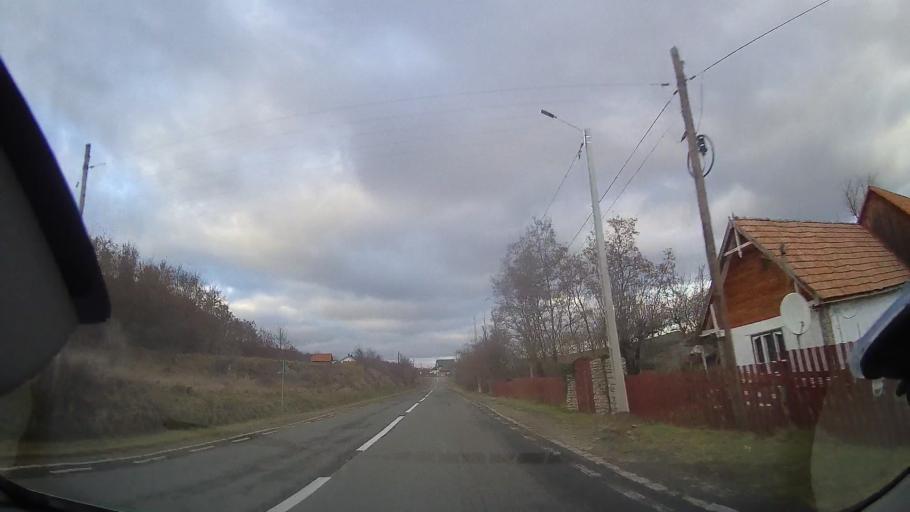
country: RO
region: Cluj
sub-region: Comuna Sancraiu
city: Sancraiu
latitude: 46.7974
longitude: 22.9944
